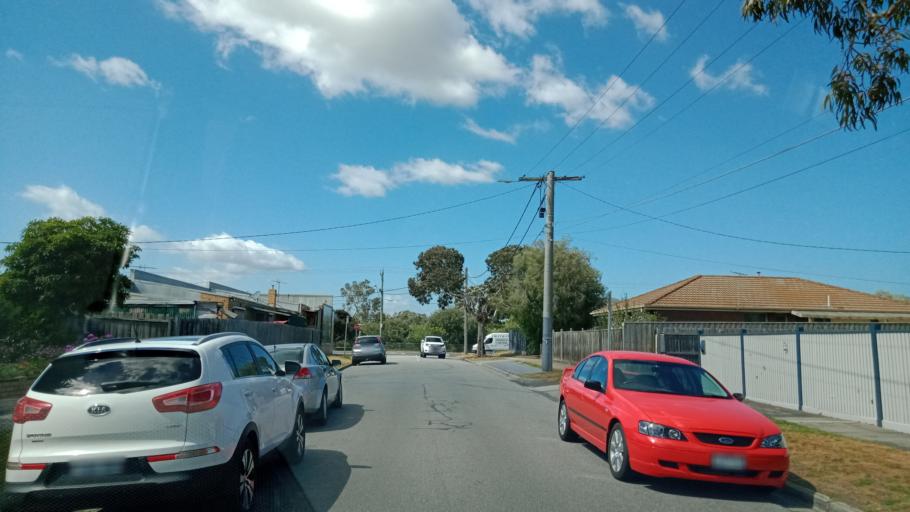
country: AU
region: Victoria
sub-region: Kingston
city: Chelsea Heights
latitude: -38.0448
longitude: 145.1356
